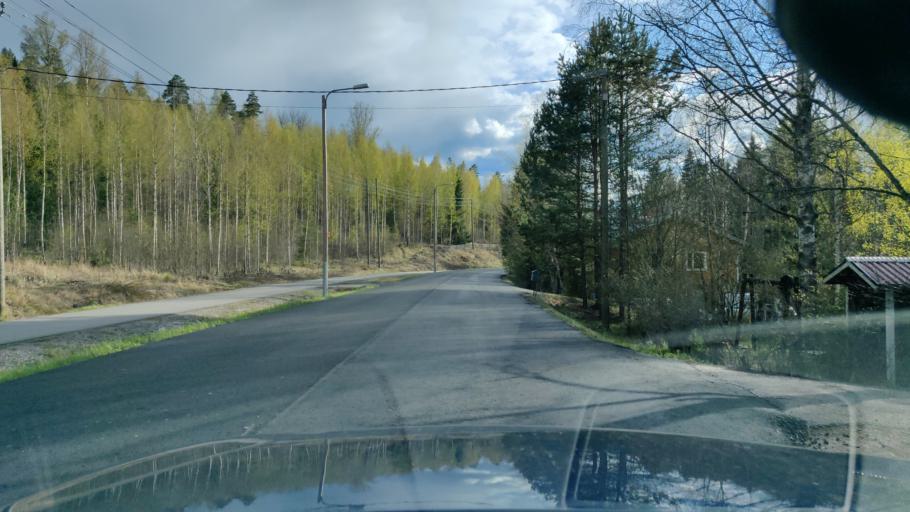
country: FI
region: Uusimaa
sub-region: Helsinki
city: Nurmijaervi
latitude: 60.3727
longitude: 24.7348
